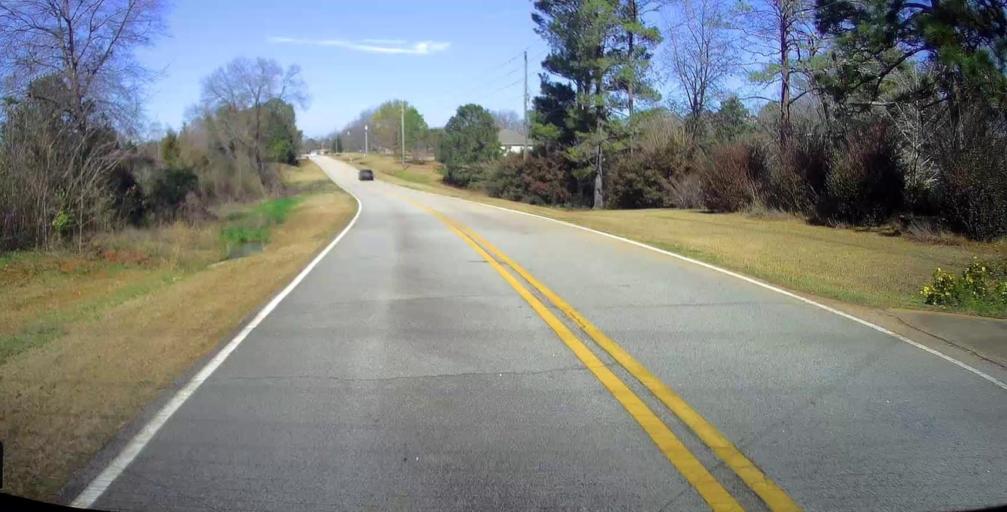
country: US
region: Georgia
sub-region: Houston County
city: Warner Robins
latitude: 32.5689
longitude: -83.6348
